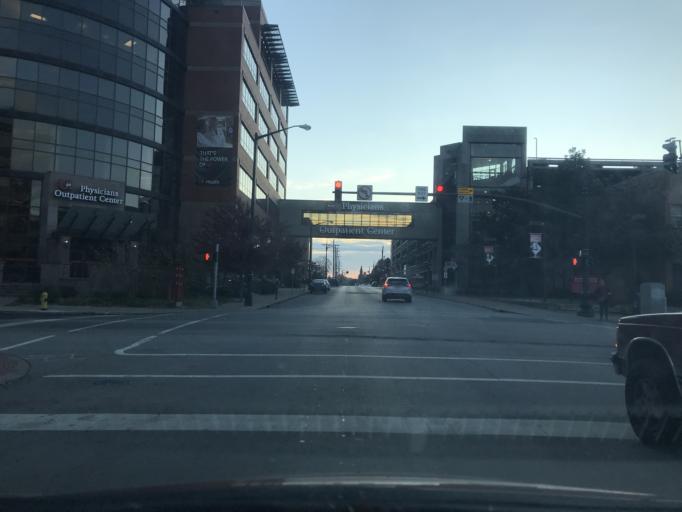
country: US
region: Kentucky
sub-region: Jefferson County
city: Louisville
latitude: 38.2478
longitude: -85.7474
